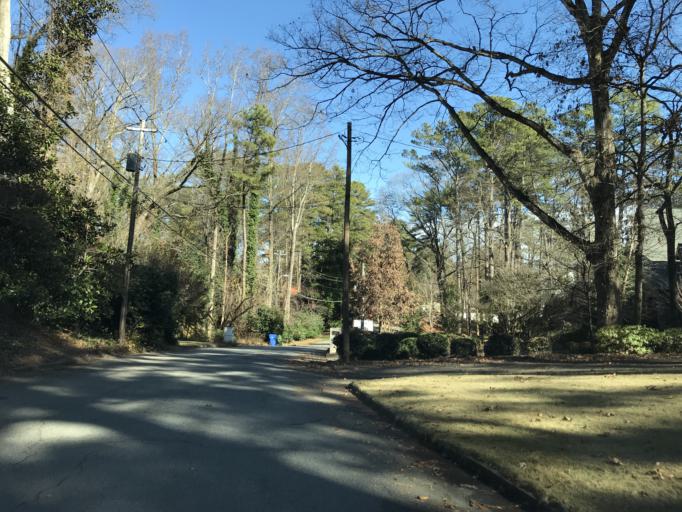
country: US
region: Georgia
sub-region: DeKalb County
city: North Atlanta
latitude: 33.8779
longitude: -84.3531
